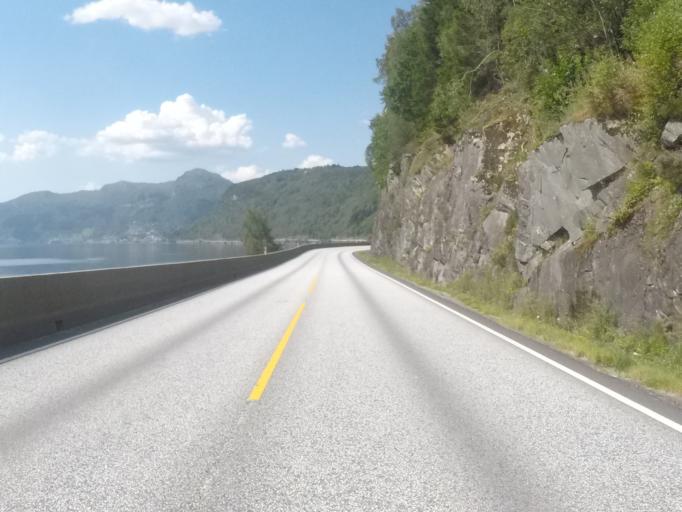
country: NO
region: Sogn og Fjordane
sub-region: Naustdal
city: Naustdal
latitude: 61.4990
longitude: 5.7750
